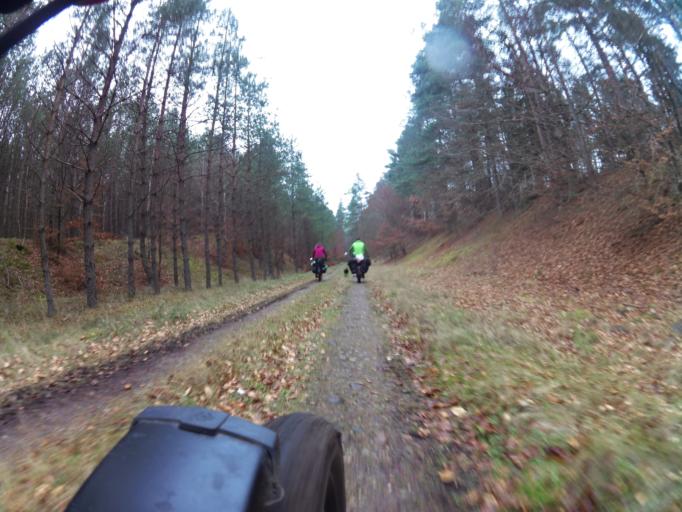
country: PL
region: West Pomeranian Voivodeship
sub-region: Powiat koszalinski
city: Polanow
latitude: 54.0403
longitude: 16.6560
